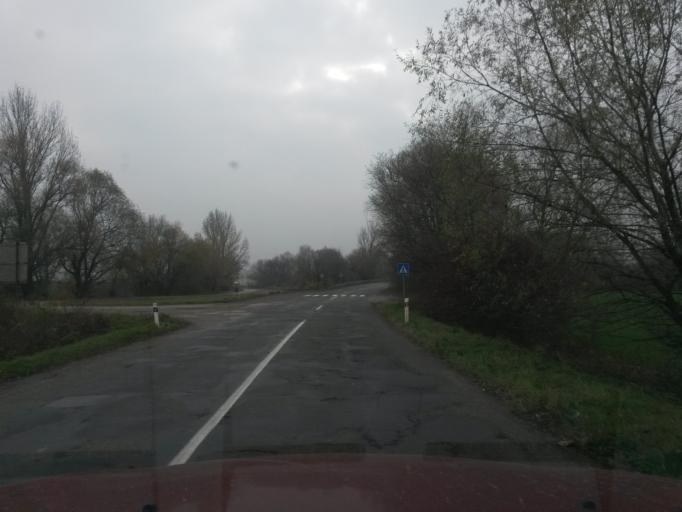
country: SK
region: Presovsky
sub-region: Okres Presov
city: Presov
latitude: 48.8601
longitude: 21.2708
